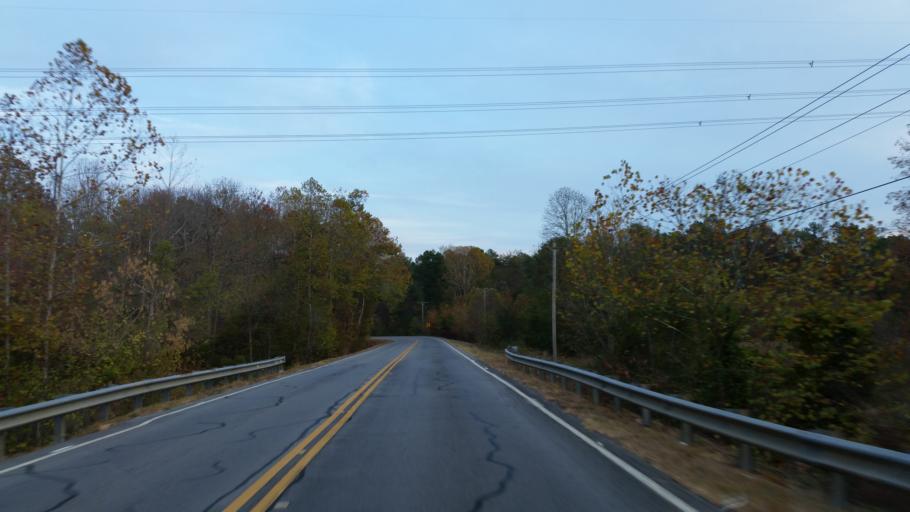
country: US
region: Georgia
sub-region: Gordon County
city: Calhoun
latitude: 34.5933
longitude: -84.8990
